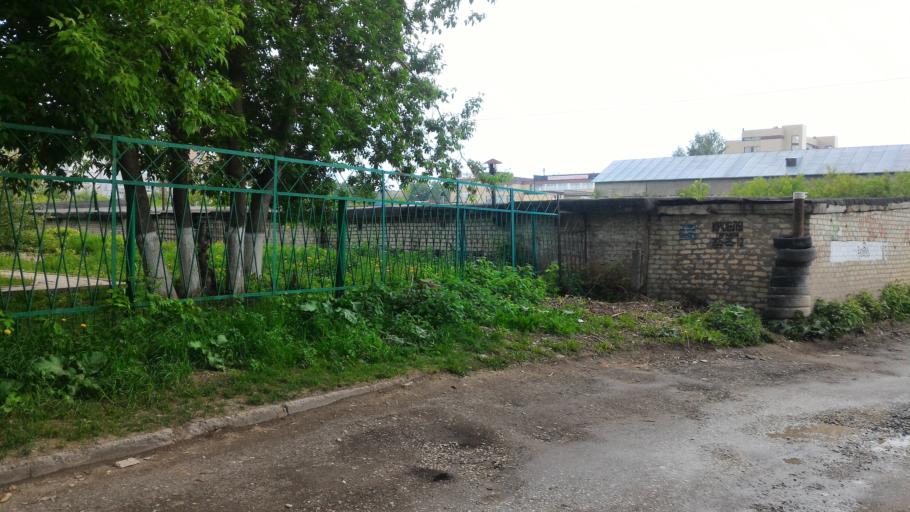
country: RU
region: Perm
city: Perm
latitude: 57.9896
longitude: 56.2119
